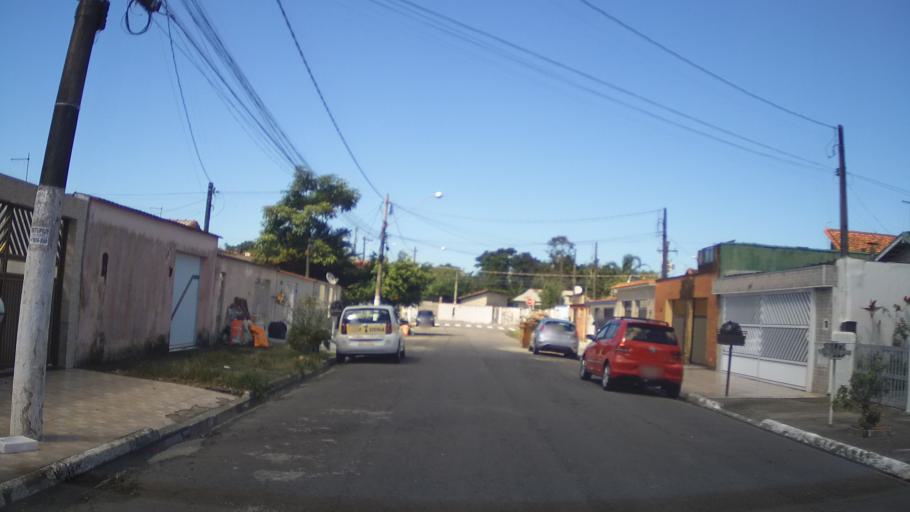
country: BR
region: Sao Paulo
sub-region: Mongagua
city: Mongagua
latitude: -24.0311
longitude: -46.5323
